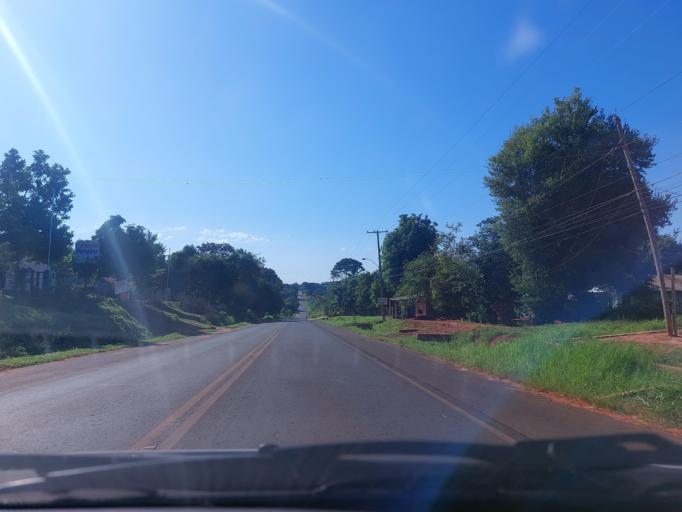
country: PY
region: San Pedro
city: Guayaybi
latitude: -24.5311
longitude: -56.4158
